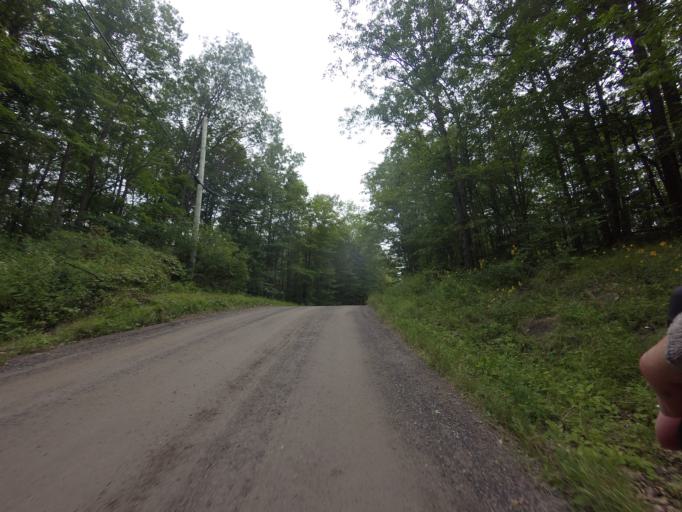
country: CA
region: Ontario
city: Kingston
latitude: 44.5572
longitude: -76.6036
